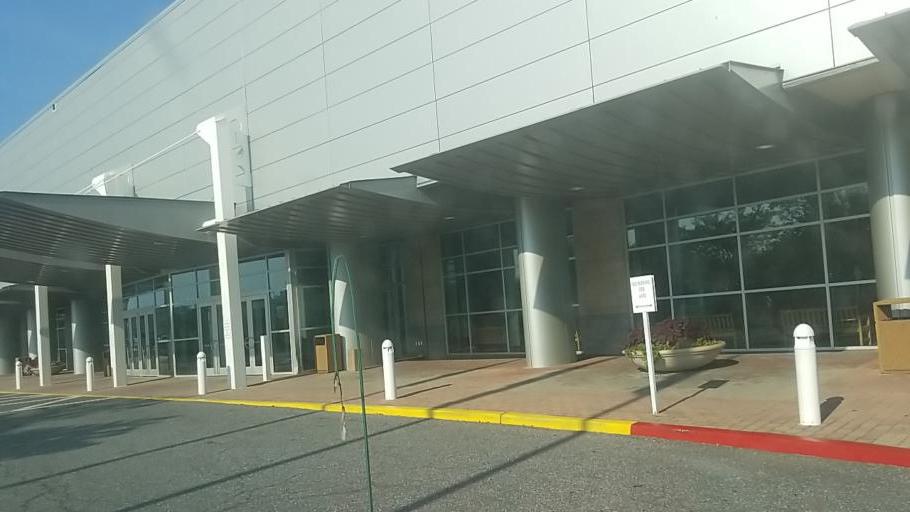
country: US
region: Maryland
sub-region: Worcester County
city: Ocean City
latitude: 38.3680
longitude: -75.0734
